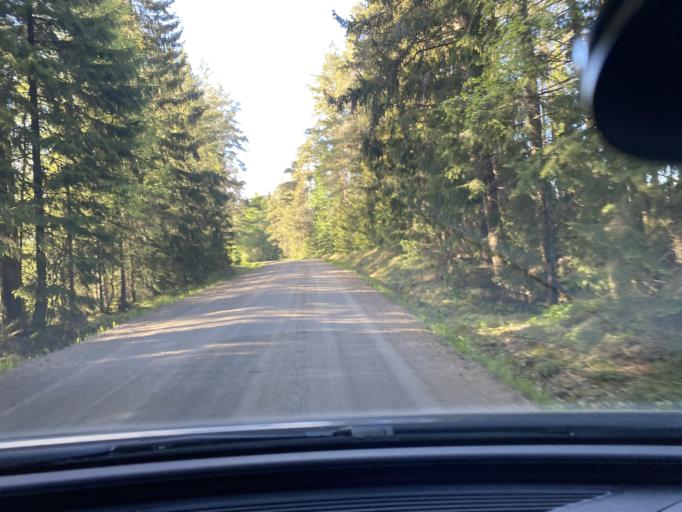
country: FI
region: Satakunta
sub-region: Pori
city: Huittinen
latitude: 61.1380
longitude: 22.8333
